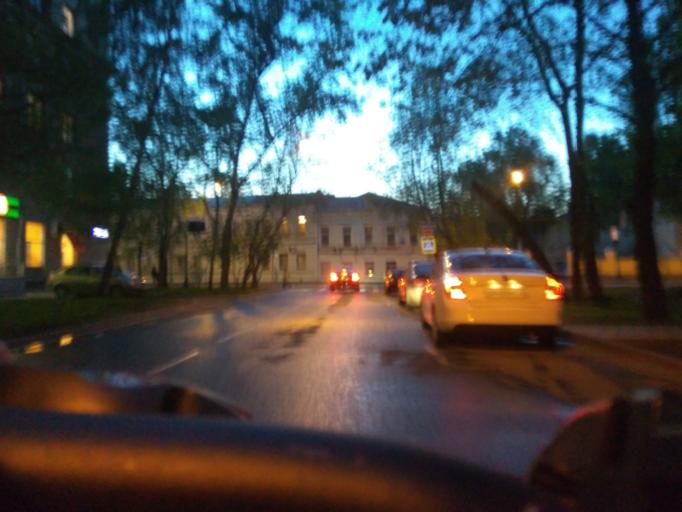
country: RU
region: Moscow
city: Taganskiy
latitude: 55.7433
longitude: 37.6622
